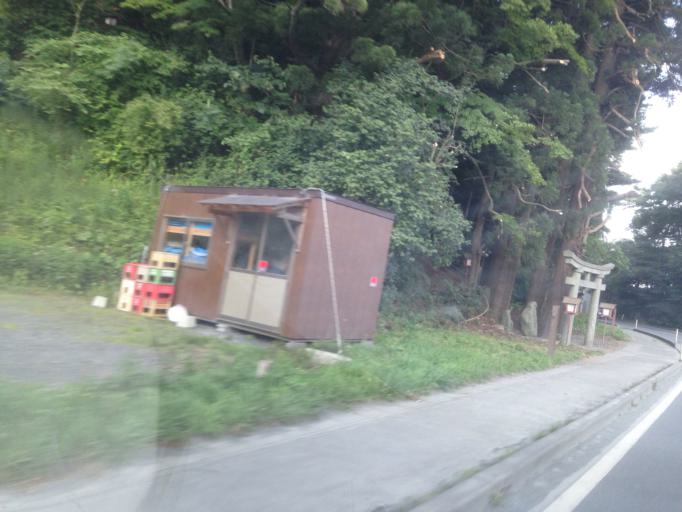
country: JP
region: Iwate
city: Otsuchi
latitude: 39.3733
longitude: 141.8892
